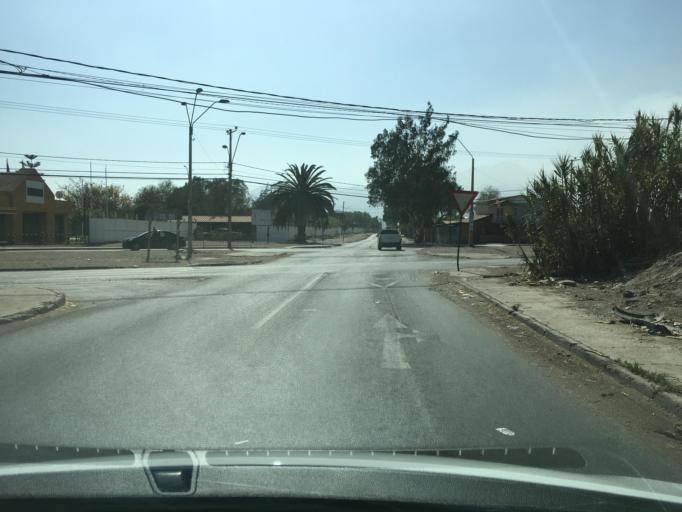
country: CL
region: Atacama
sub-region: Provincia de Copiapo
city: Copiapo
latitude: -27.4127
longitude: -70.2828
